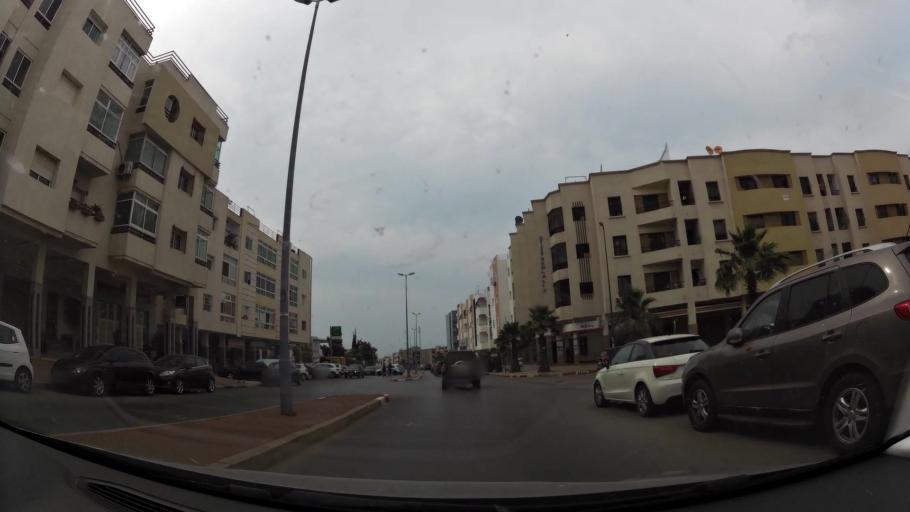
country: MA
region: Rabat-Sale-Zemmour-Zaer
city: Sale
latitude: 34.0302
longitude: -6.8015
